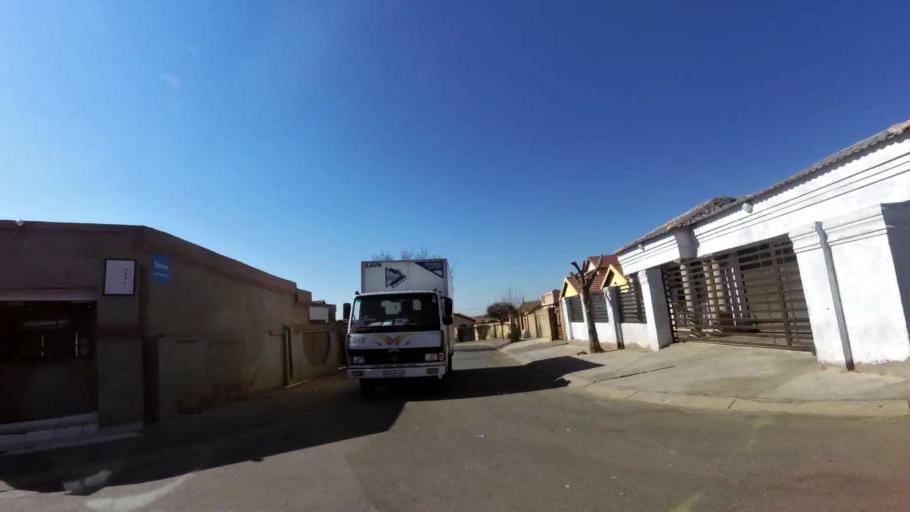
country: ZA
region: Gauteng
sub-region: City of Johannesburg Metropolitan Municipality
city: Johannesburg
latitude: -26.2494
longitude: 27.9814
